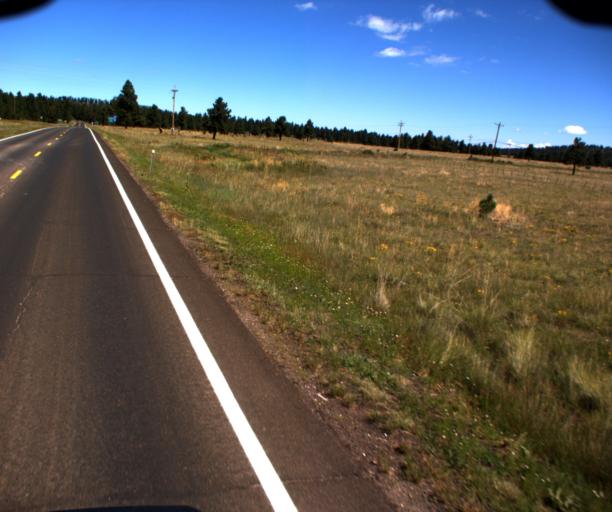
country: US
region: Arizona
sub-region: Apache County
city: Eagar
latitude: 34.0289
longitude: -109.4507
